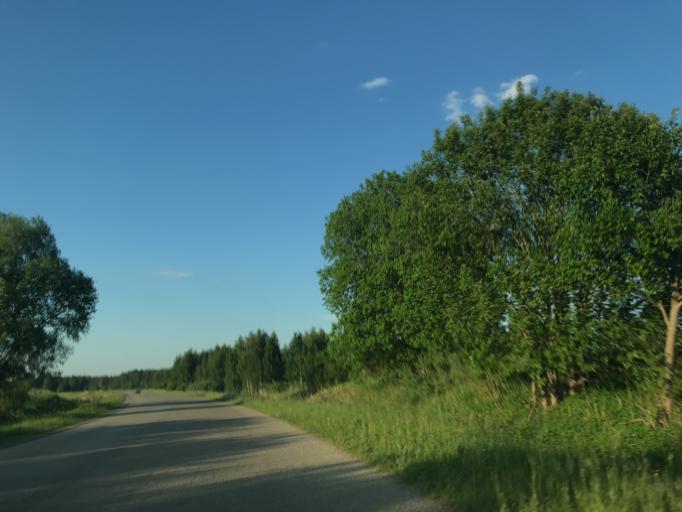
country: LV
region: Baldone
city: Baldone
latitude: 56.7088
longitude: 24.3633
